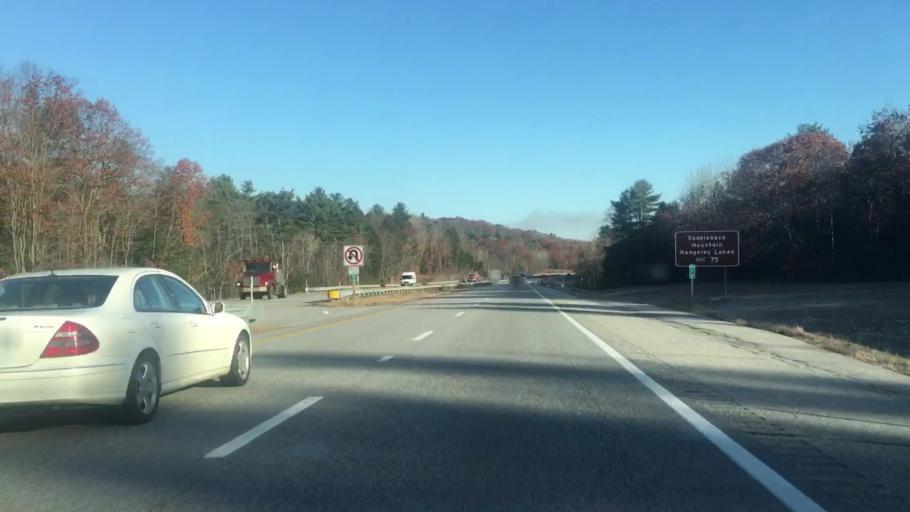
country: US
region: Maine
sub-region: Cumberland County
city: New Gloucester
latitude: 44.0019
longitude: -70.3067
